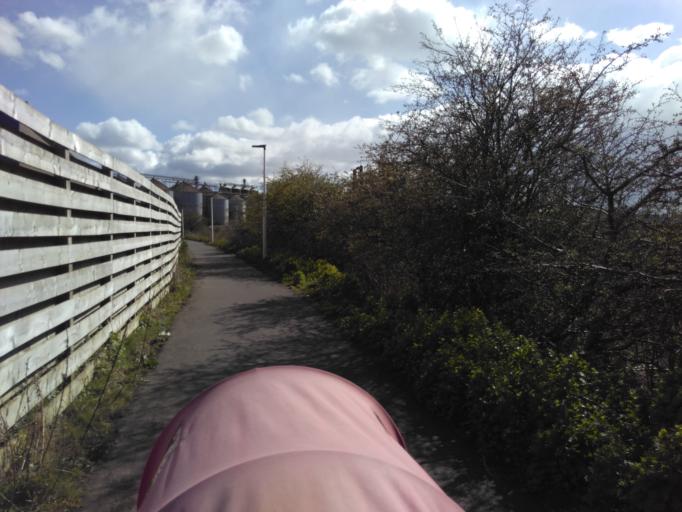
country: GB
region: Scotland
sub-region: Midlothian
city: Loanhead
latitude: 55.8877
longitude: -3.1475
